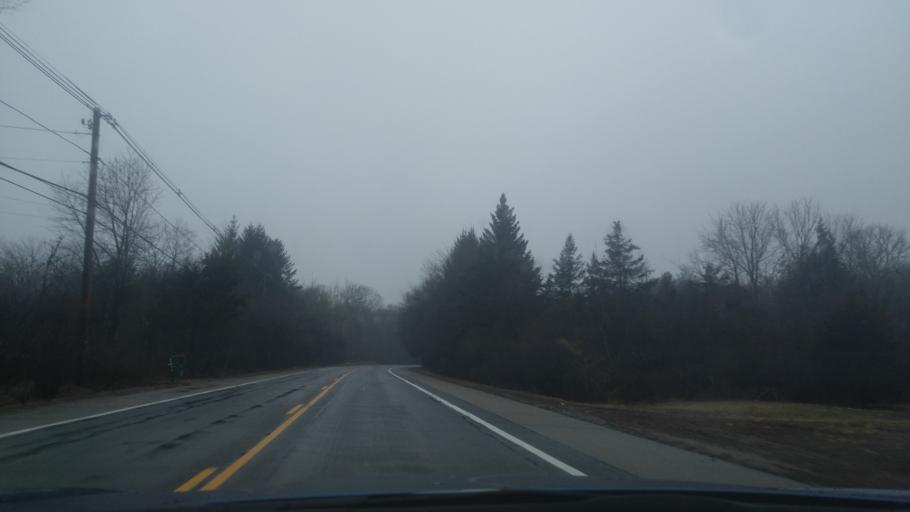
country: US
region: Rhode Island
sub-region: Washington County
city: Kingston
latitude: 41.4812
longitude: -71.5910
